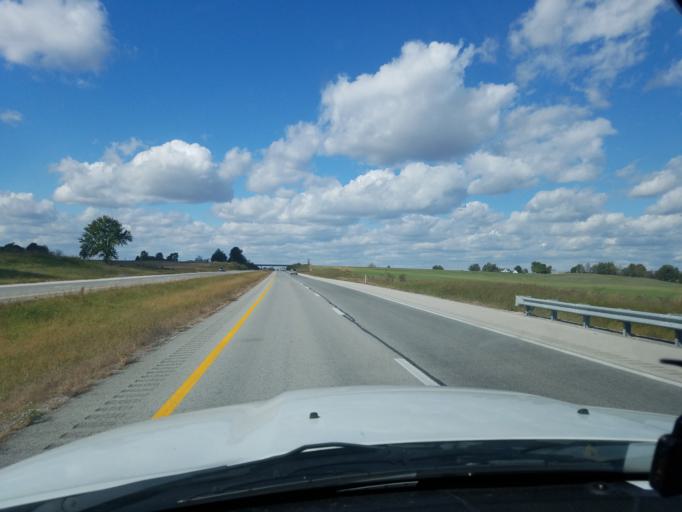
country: US
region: Kentucky
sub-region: Daviess County
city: Masonville
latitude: 37.6572
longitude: -87.0078
